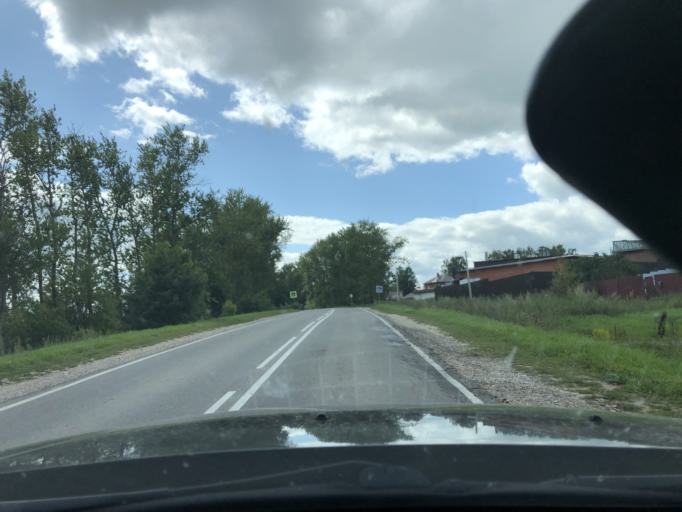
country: RU
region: Tula
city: Revyakino
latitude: 54.3594
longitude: 37.6379
